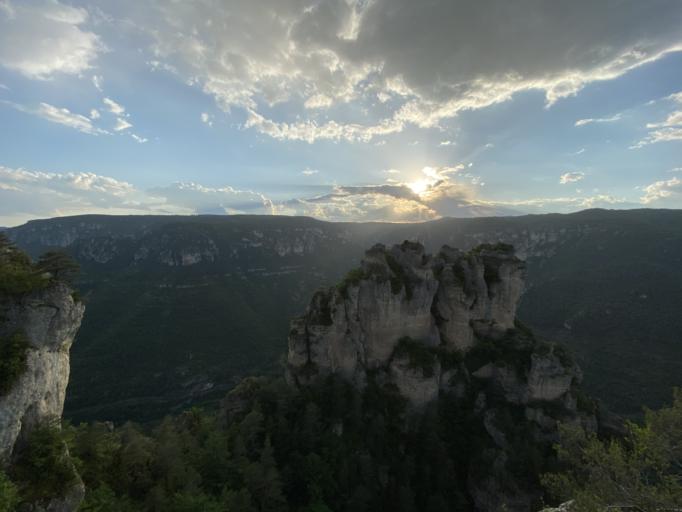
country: FR
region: Midi-Pyrenees
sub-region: Departement de l'Aveyron
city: Millau
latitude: 44.2198
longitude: 3.2311
